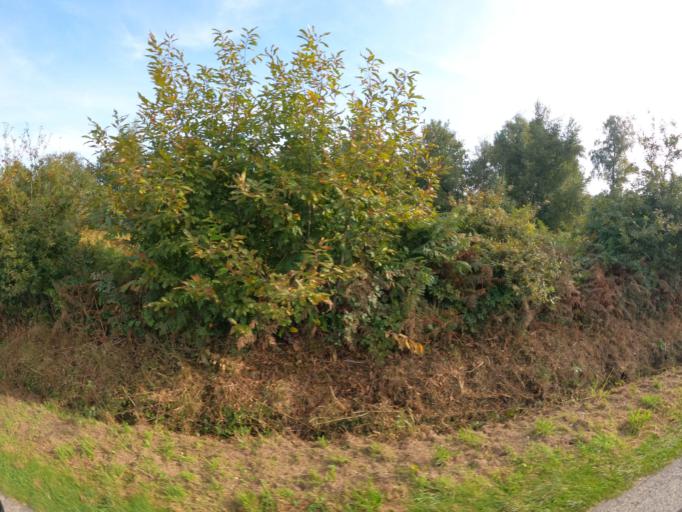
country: FR
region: Brittany
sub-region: Departement du Morbihan
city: Ploermel
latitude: 47.8728
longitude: -2.4066
